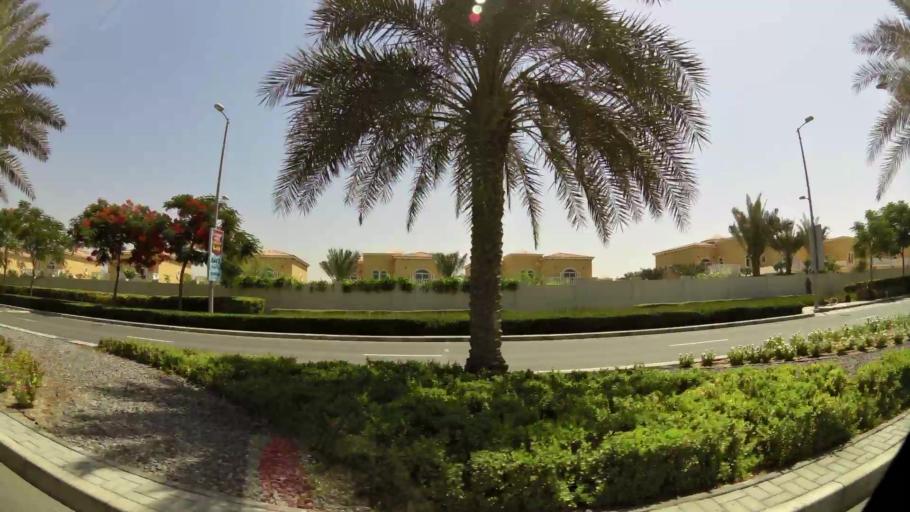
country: AE
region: Dubai
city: Dubai
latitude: 25.0535
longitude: 55.1467
